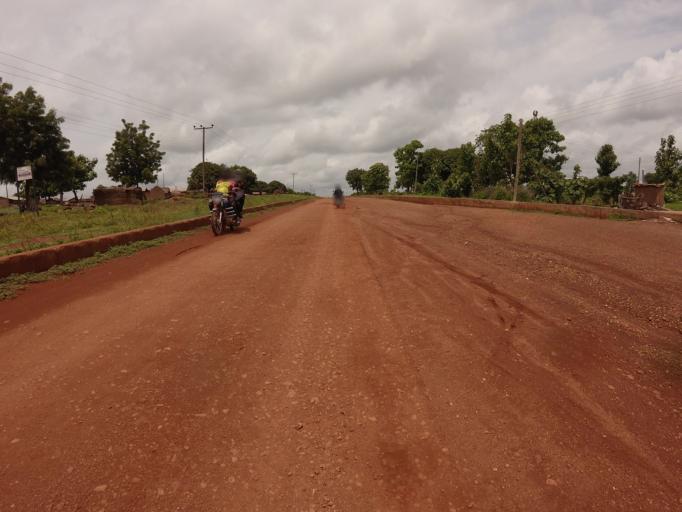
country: GH
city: Kpandae
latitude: 8.4537
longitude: 0.3461
